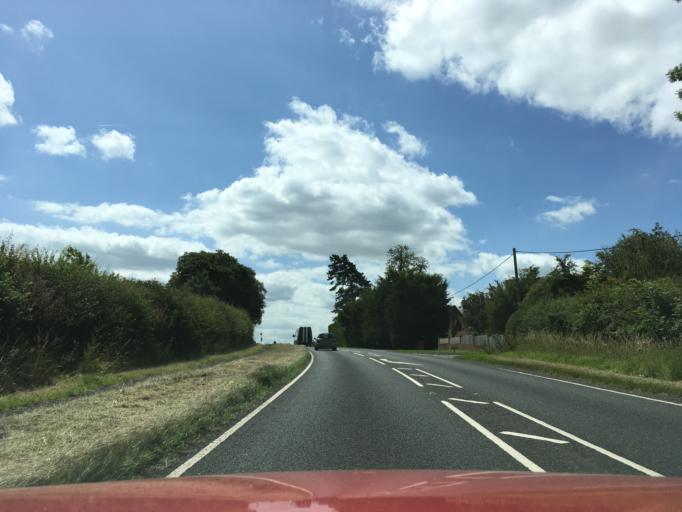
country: GB
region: England
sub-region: Buckinghamshire
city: Aylesbury
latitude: 51.8590
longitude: -0.8302
